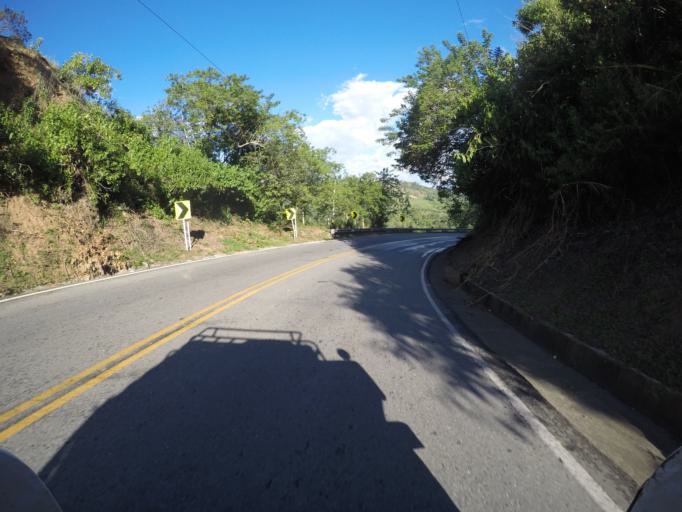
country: CO
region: Valle del Cauca
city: Cartago
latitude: 4.7180
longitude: -75.8580
